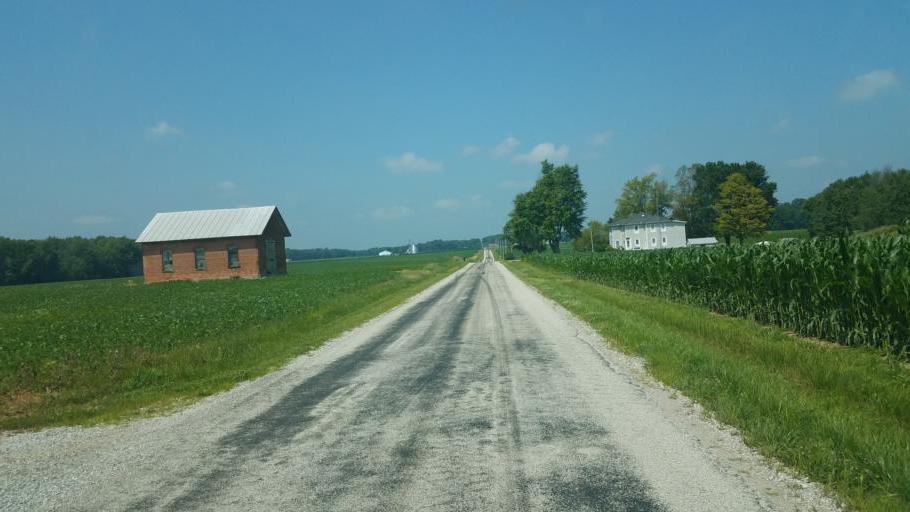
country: US
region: Ohio
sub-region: Huron County
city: Willard
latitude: 40.9800
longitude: -82.8562
